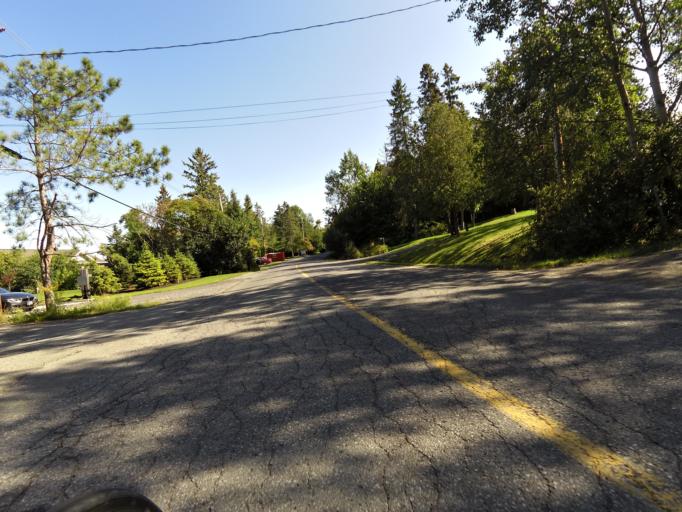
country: CA
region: Ontario
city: Bells Corners
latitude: 45.4638
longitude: -75.9735
